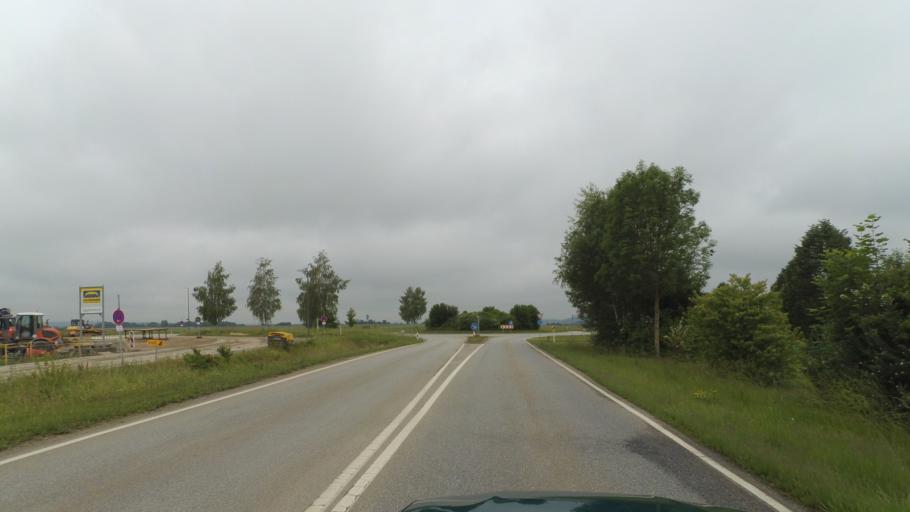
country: DE
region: Bavaria
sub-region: Lower Bavaria
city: Geiselhoring
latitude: 48.8138
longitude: 12.3895
